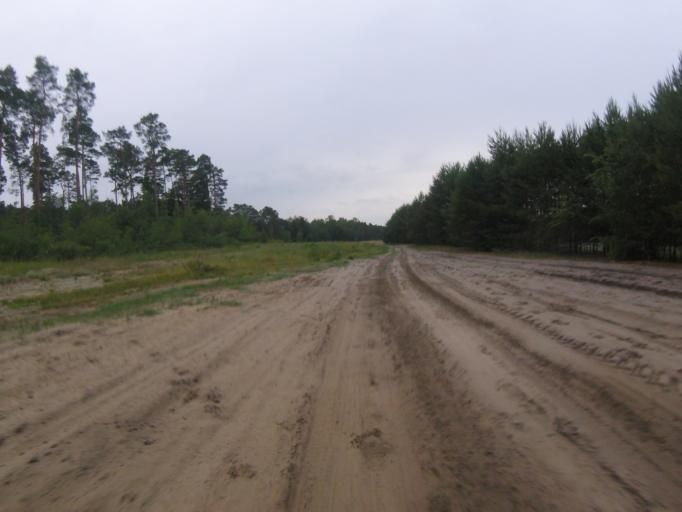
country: DE
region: Brandenburg
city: Gross Koris
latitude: 52.1955
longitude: 13.6472
